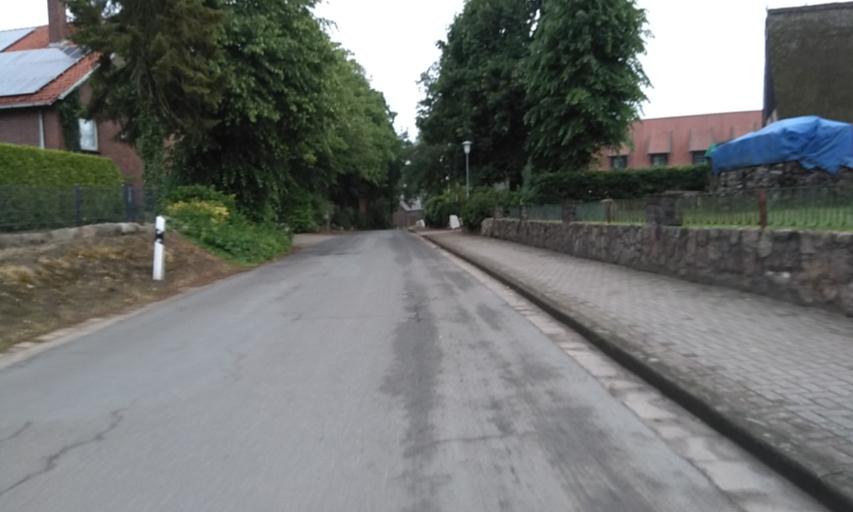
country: DE
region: Lower Saxony
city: Deinste
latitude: 53.5266
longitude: 9.4432
